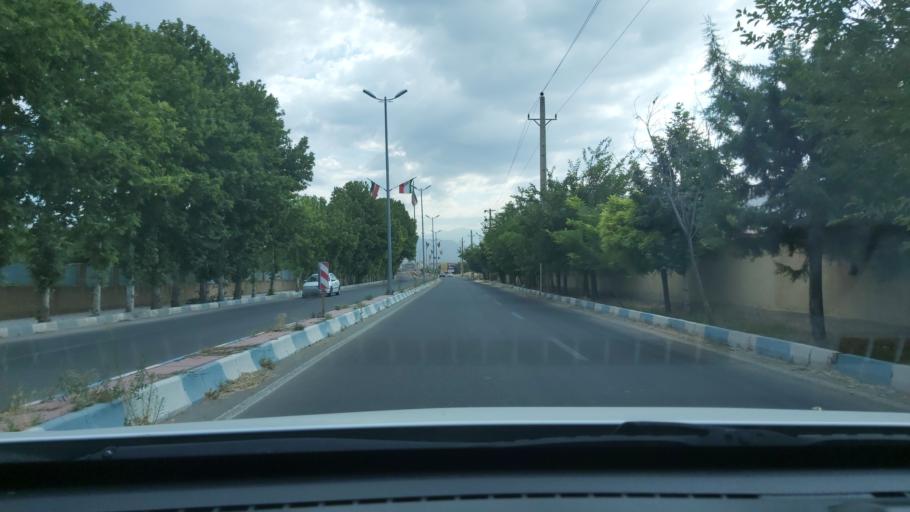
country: IR
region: Alborz
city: Hashtgerd
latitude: 35.9413
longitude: 50.7687
